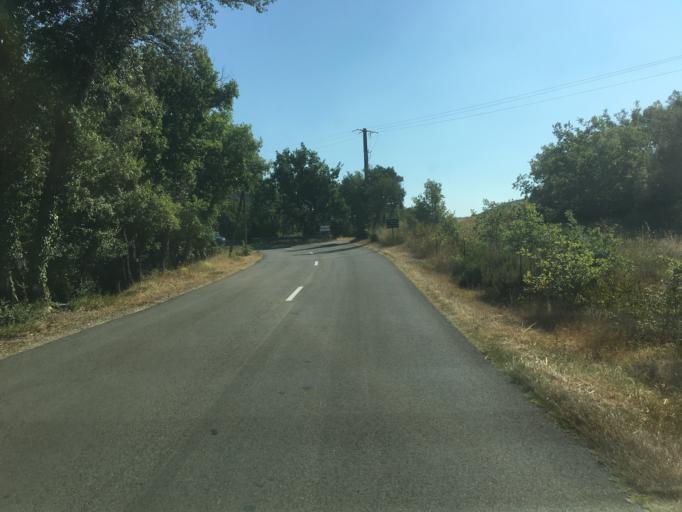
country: FR
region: Provence-Alpes-Cote d'Azur
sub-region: Departement des Alpes-de-Haute-Provence
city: Volx
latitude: 43.8273
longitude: 5.8568
